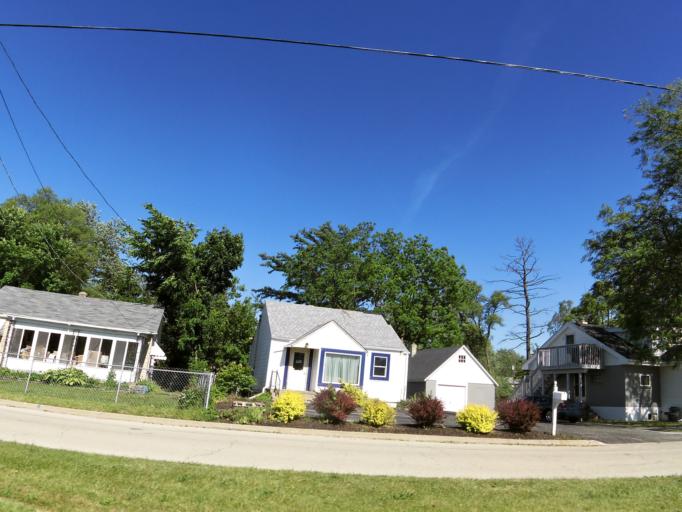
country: US
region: Illinois
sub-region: Winnebago County
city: Machesney Park
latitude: 42.3374
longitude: -89.0536
